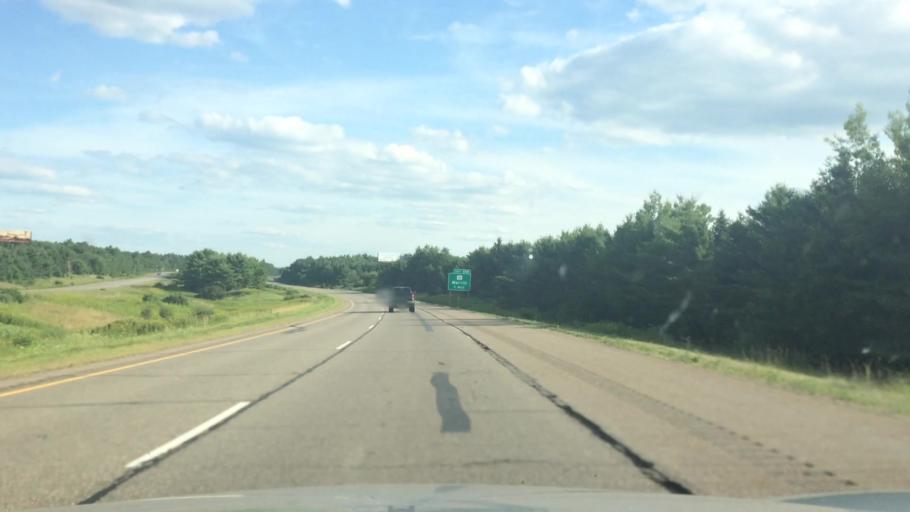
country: US
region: Wisconsin
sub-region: Lincoln County
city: Merrill
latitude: 45.1538
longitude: -89.6447
